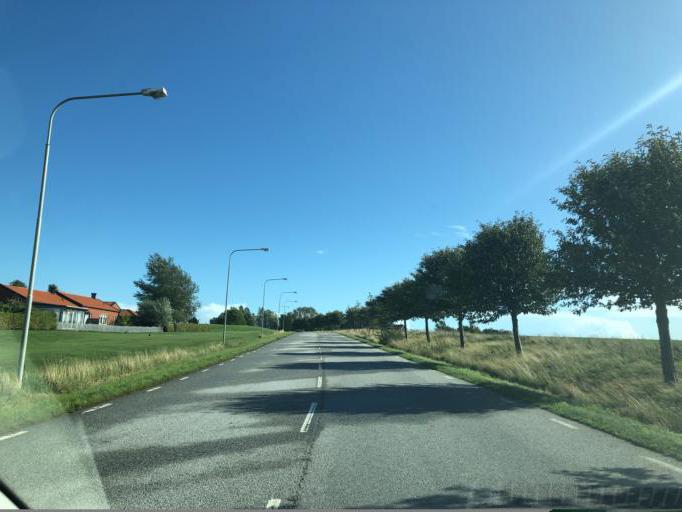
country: SE
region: Skane
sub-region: Helsingborg
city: Glumslov
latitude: 55.9368
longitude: 12.8070
